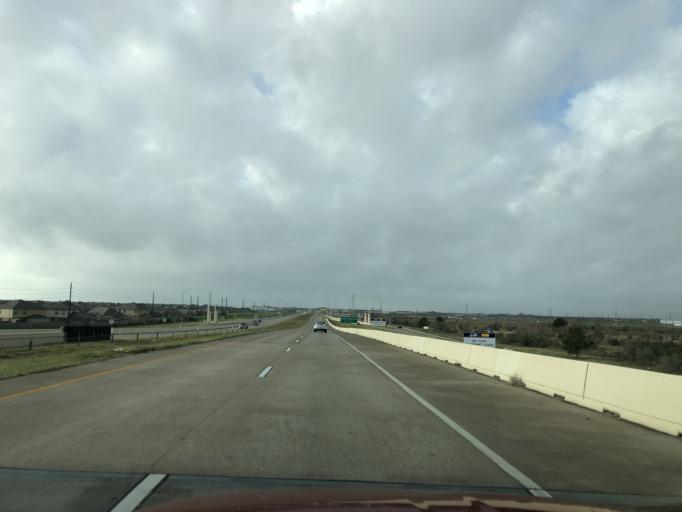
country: US
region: Texas
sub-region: Harris County
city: Katy
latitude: 29.8311
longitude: -95.7612
